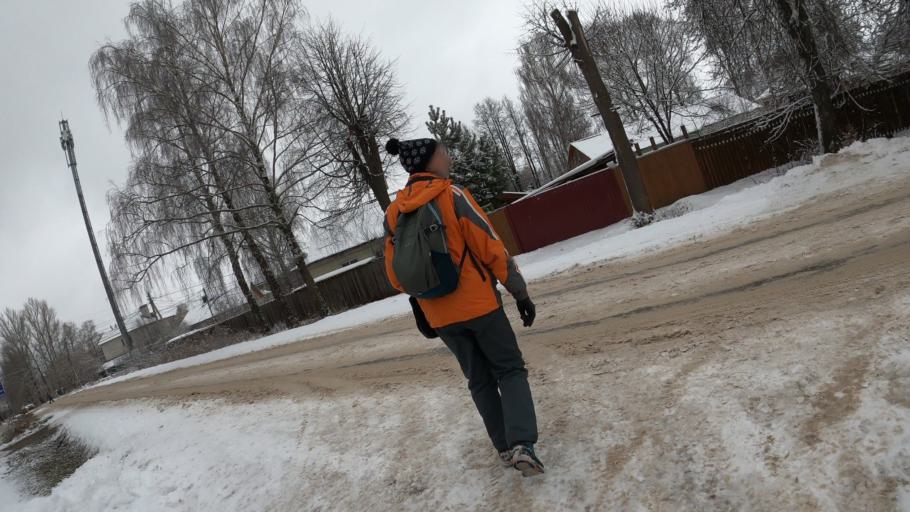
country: RU
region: Jaroslavl
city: Pereslavl'-Zalesskiy
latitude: 56.7492
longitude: 38.8645
